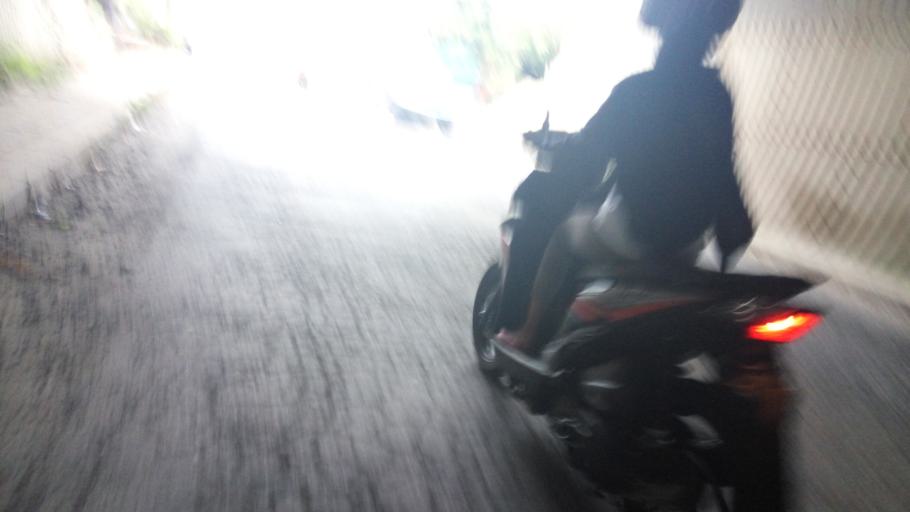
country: ID
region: Central Java
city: Semarang
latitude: -7.0133
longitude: 110.3850
